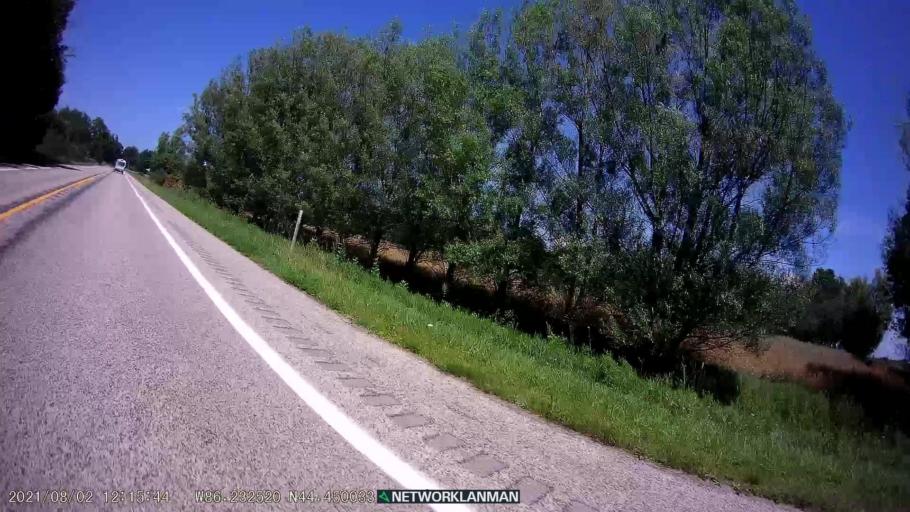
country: US
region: Michigan
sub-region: Benzie County
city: Frankfort
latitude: 44.4502
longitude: -86.2325
